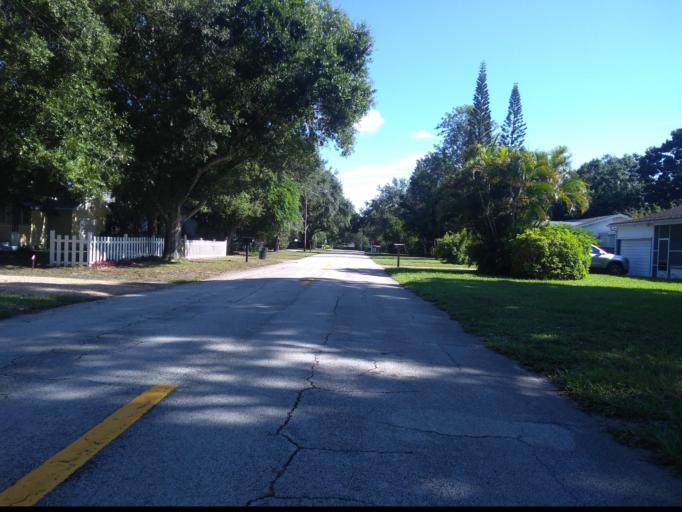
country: US
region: Florida
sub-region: Indian River County
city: Vero Beach
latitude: 27.6370
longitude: -80.4122
